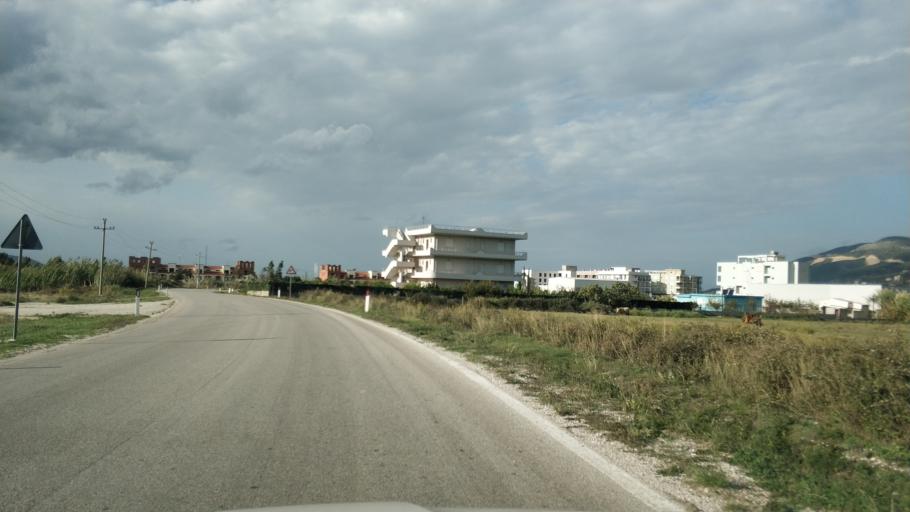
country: AL
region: Vlore
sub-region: Rrethi i Vlores
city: Orikum
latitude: 40.3361
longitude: 19.4765
